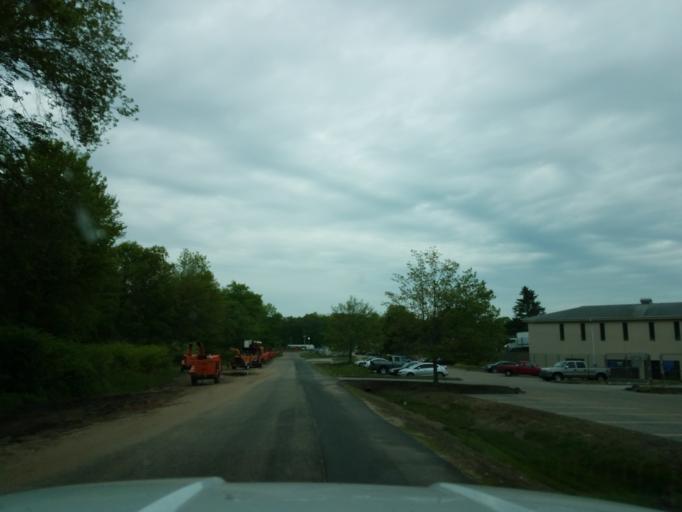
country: US
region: Connecticut
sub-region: Tolland County
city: South Coventry
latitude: 41.8128
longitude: -72.2988
